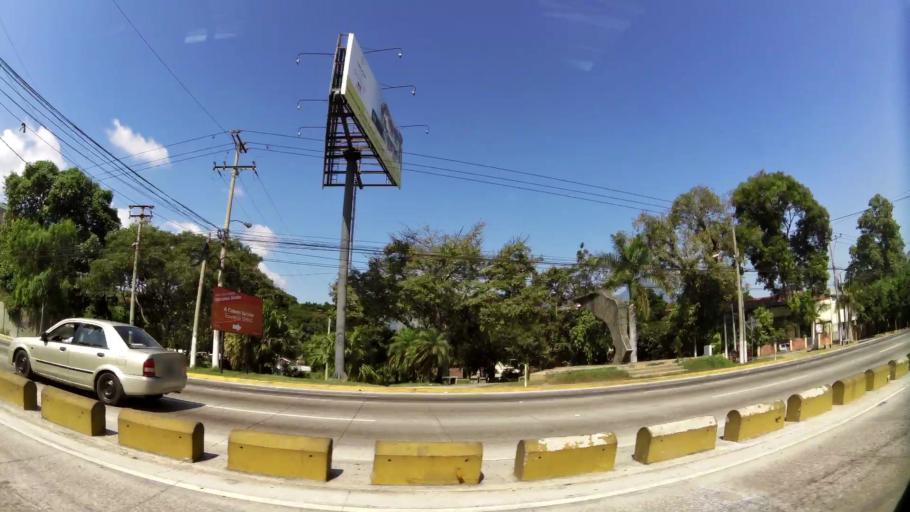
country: SV
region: La Libertad
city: Antiguo Cuscatlan
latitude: 13.6814
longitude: -89.2427
